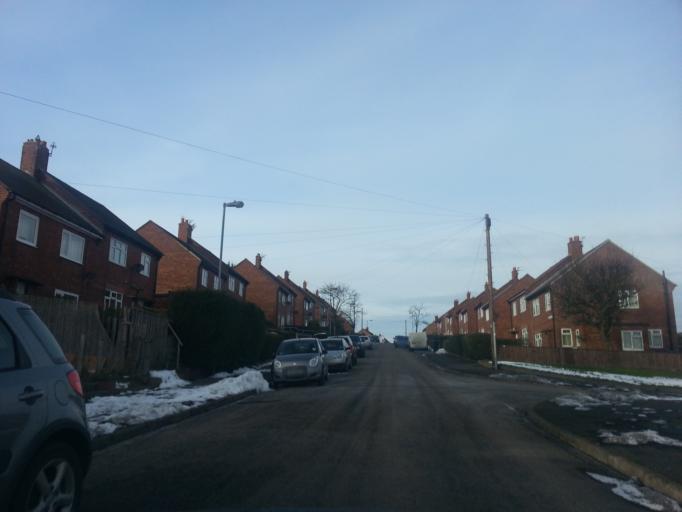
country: GB
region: England
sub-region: County Durham
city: Crook
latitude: 54.7143
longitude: -1.7571
